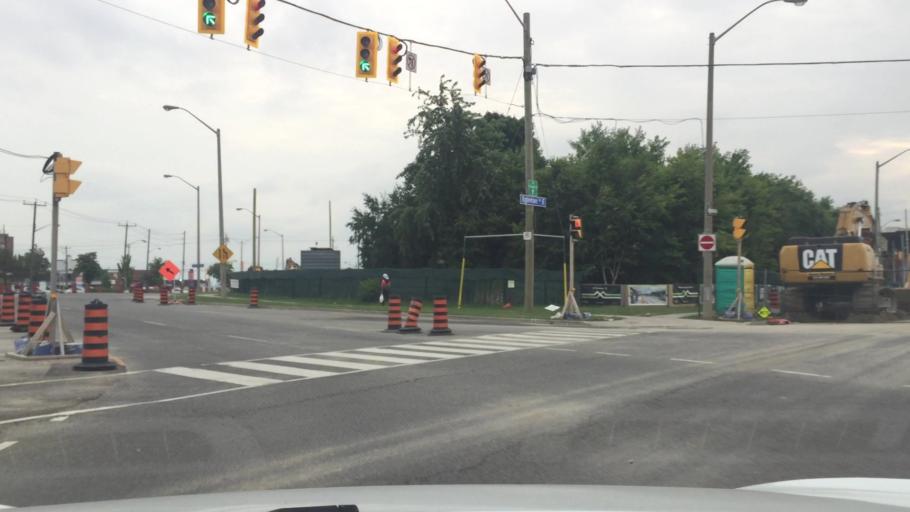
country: CA
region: Ontario
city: Scarborough
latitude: 43.7249
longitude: -79.3006
